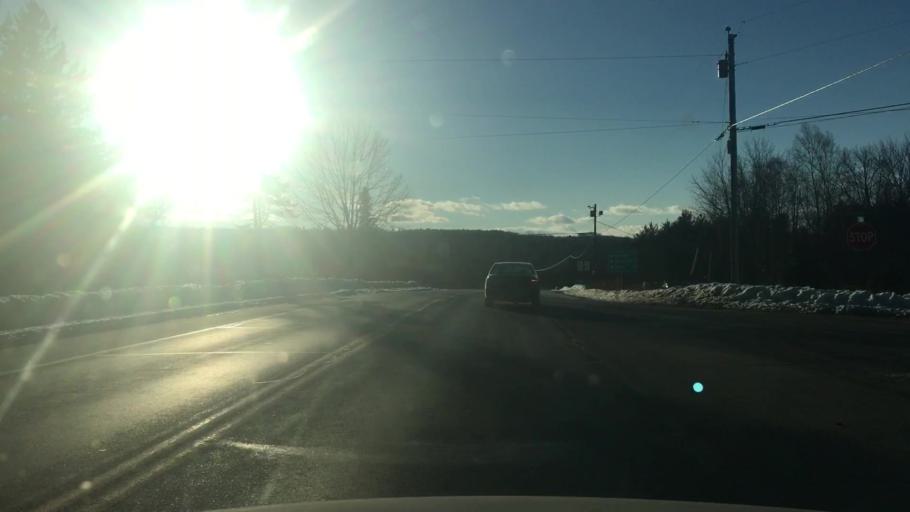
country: US
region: Maine
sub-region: Franklin County
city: New Sharon
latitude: 44.6376
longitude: -69.9991
